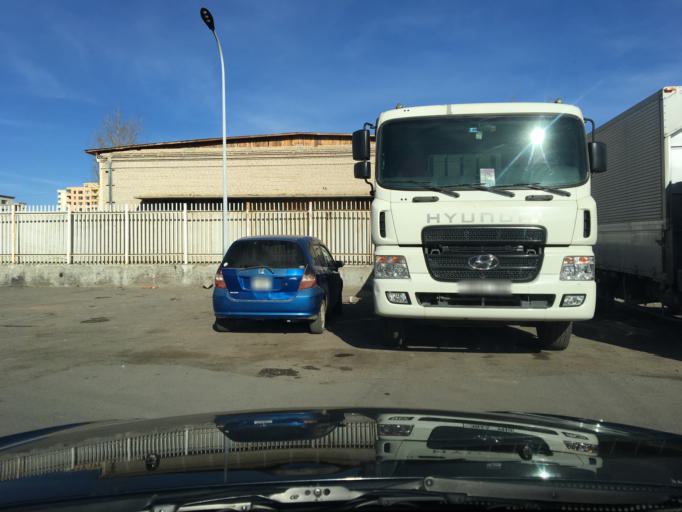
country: MN
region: Ulaanbaatar
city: Ulaanbaatar
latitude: 47.8952
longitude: 106.8978
